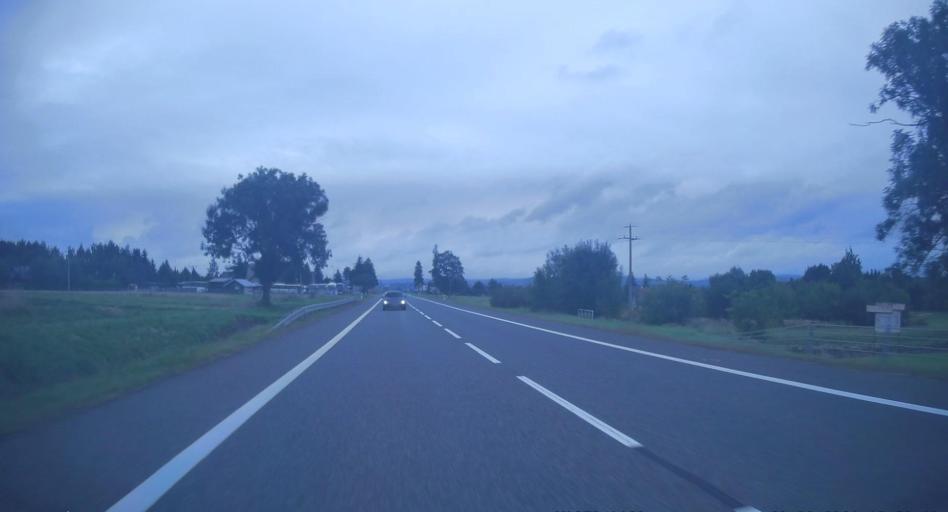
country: PL
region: Lesser Poland Voivodeship
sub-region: Powiat wielicki
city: Szarow
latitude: 49.9779
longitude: 20.2707
